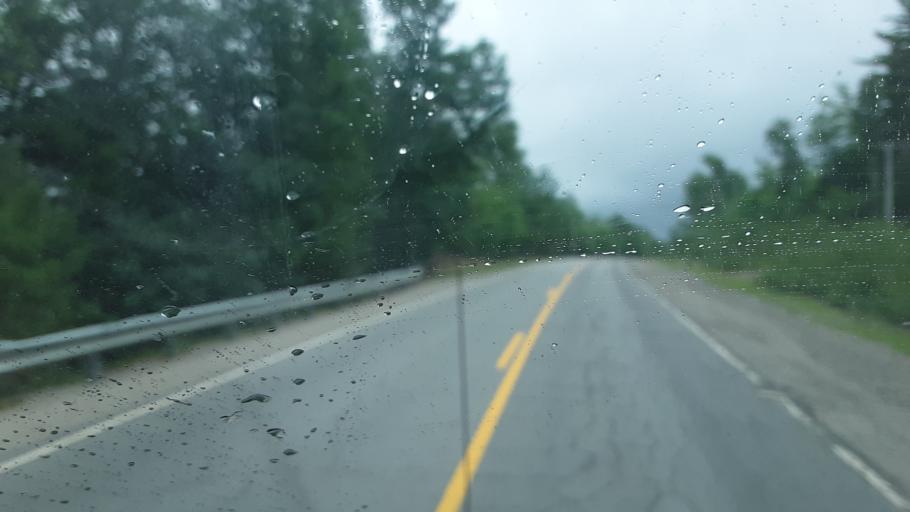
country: US
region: Maine
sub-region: Penobscot County
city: Millinocket
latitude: 45.6920
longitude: -68.7892
